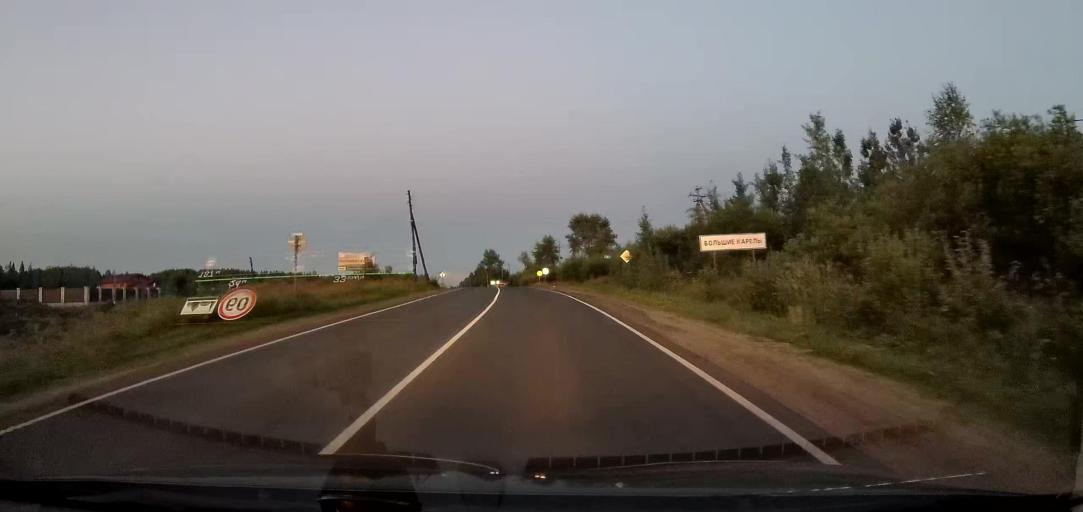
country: RU
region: Arkhangelskaya
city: Uyemskiy
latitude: 64.4477
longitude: 40.9464
